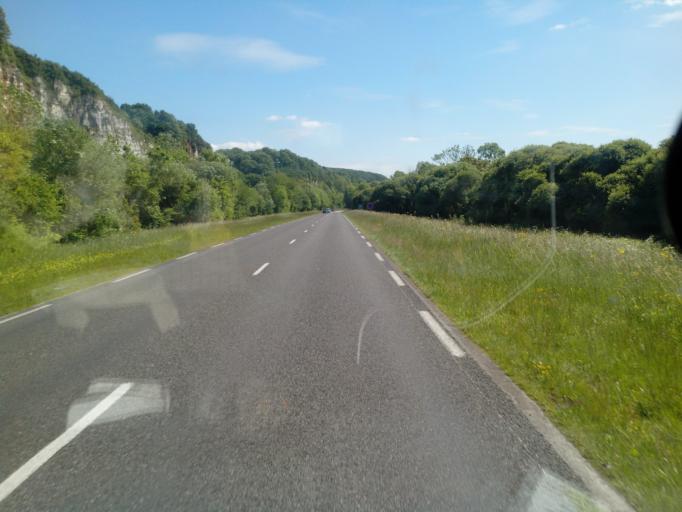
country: FR
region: Haute-Normandie
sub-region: Departement de la Seine-Maritime
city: Tancarville
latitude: 49.4371
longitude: 0.4228
